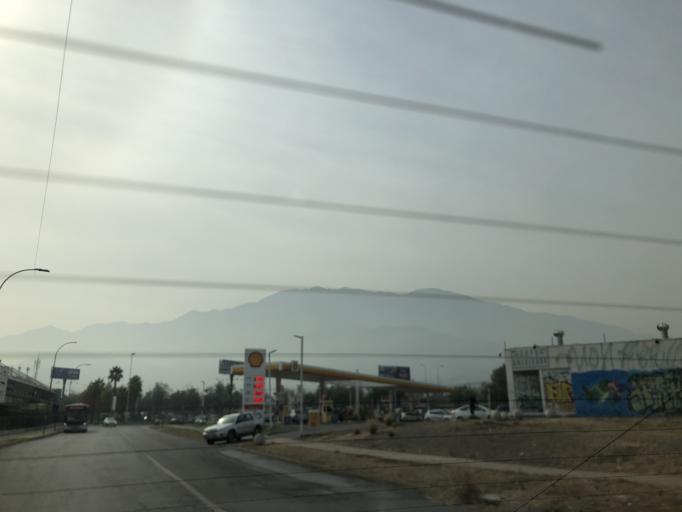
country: CL
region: Santiago Metropolitan
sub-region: Provincia de Cordillera
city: Puente Alto
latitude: -33.5715
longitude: -70.5563
